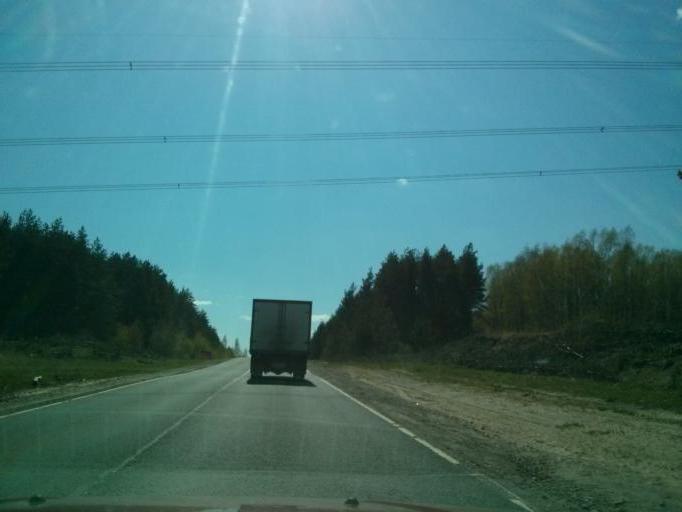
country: RU
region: Nizjnij Novgorod
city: Vorsma
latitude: 56.0246
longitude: 43.3557
